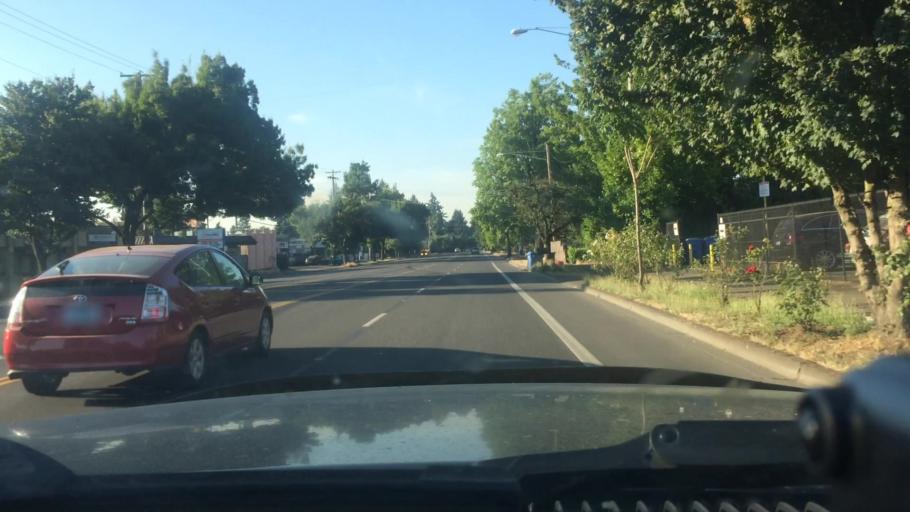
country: US
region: Oregon
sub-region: Lane County
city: Eugene
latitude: 44.0777
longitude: -123.1206
